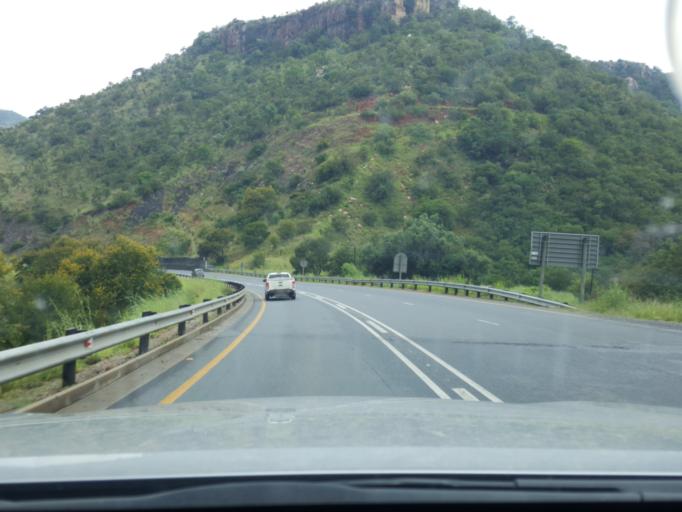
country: ZA
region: Mpumalanga
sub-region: Nkangala District Municipality
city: Belfast
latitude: -25.6425
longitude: 30.3462
